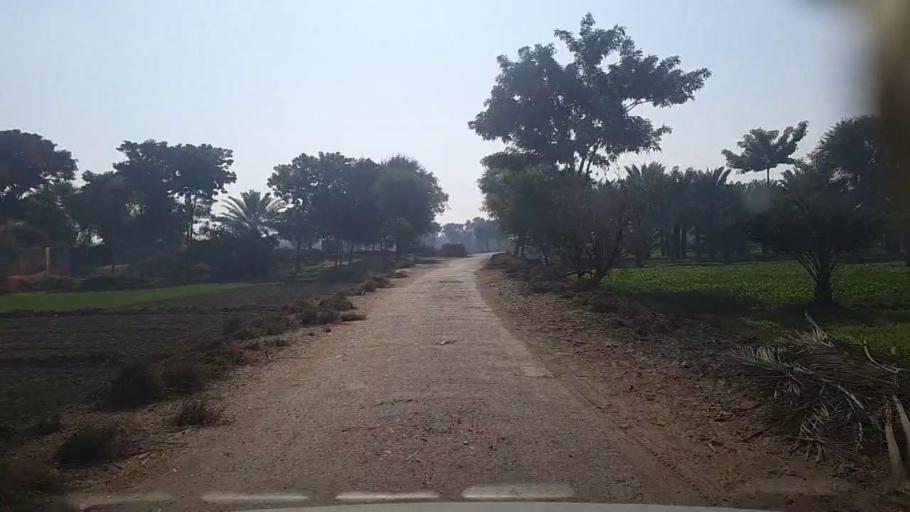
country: PK
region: Sindh
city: Kandiari
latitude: 26.9904
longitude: 68.4694
